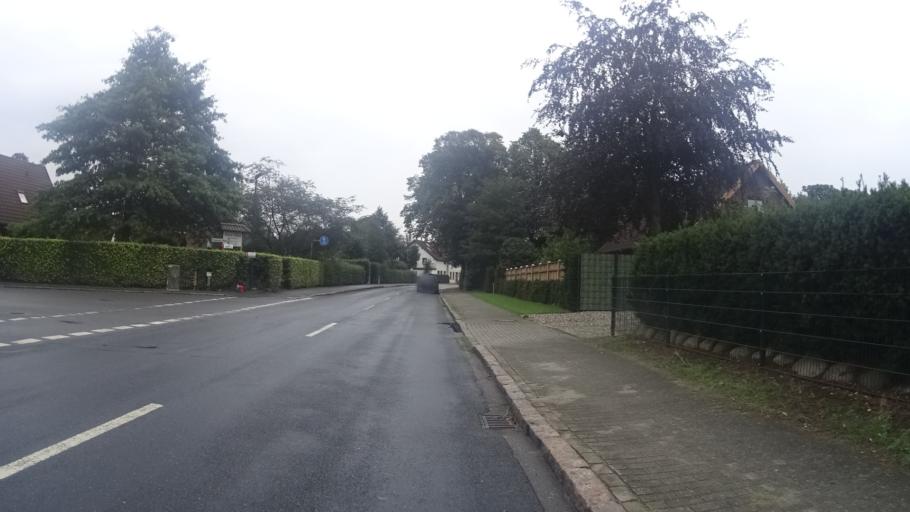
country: DE
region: Schleswig-Holstein
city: Bevern
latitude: 53.7563
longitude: 9.7686
